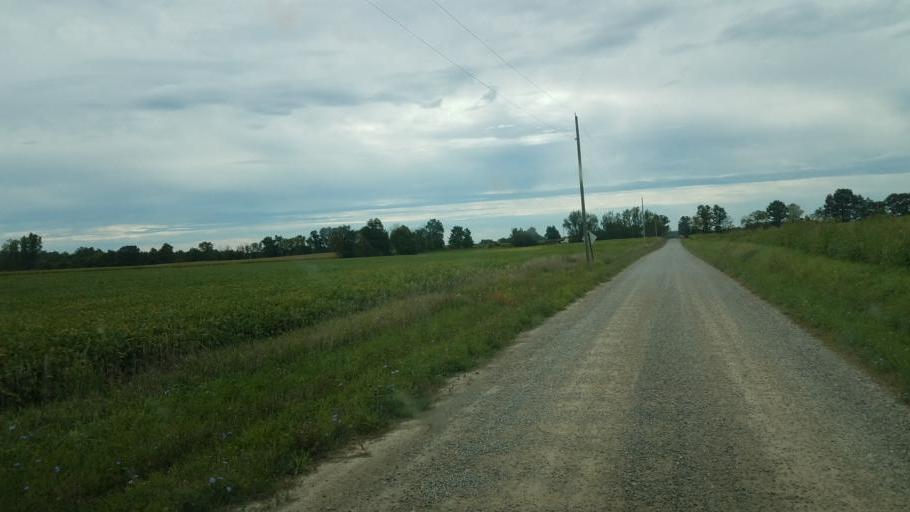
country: US
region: Ohio
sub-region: Knox County
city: Centerburg
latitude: 40.3341
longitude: -82.7165
